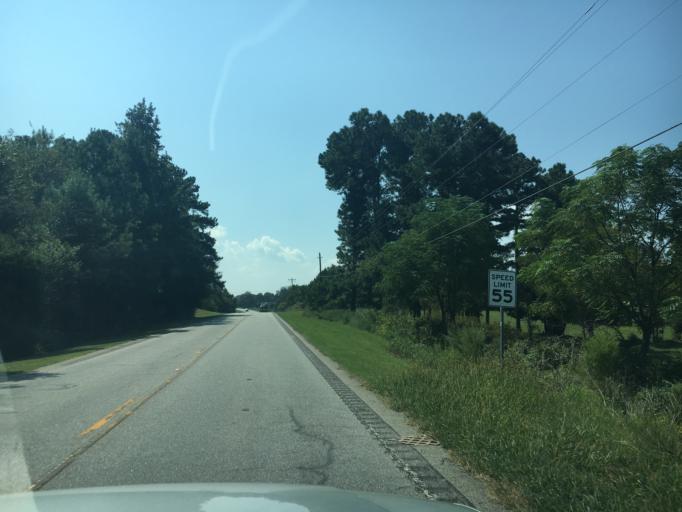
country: US
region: South Carolina
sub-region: Anderson County
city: Centerville
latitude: 34.4918
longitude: -82.7794
